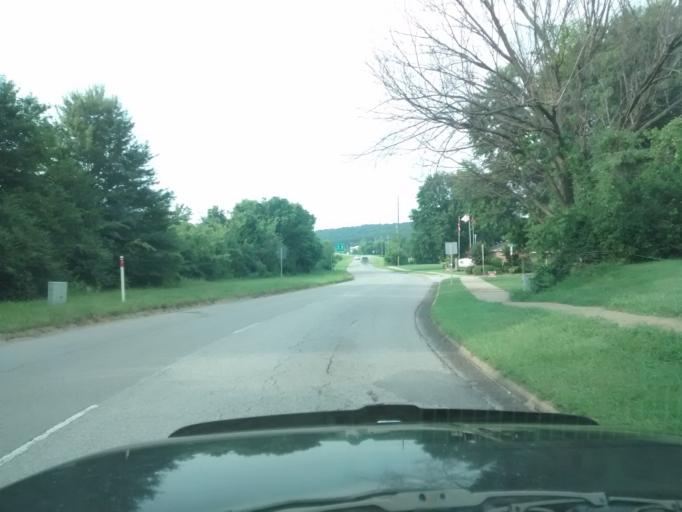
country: US
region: Arkansas
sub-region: Washington County
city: Fayetteville
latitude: 36.0771
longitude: -94.2024
